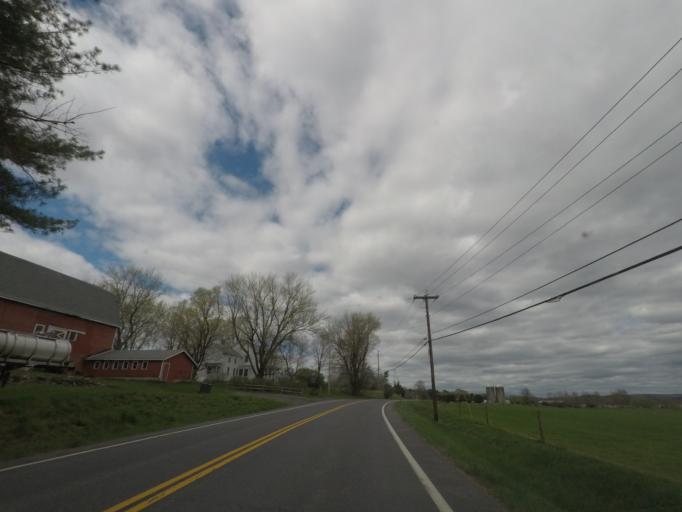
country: US
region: New York
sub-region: Columbia County
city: Philmont
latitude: 42.2733
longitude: -73.6615
